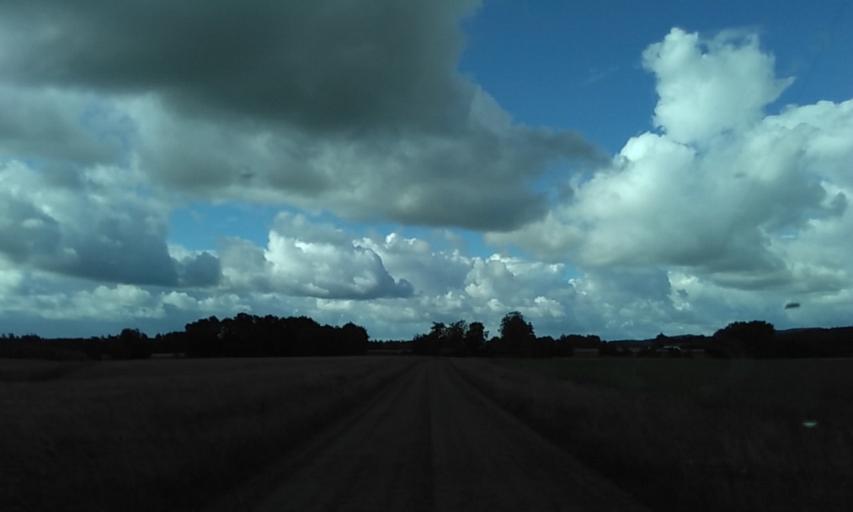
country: SE
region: Vaestra Goetaland
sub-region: Vargarda Kommun
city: Jonstorp
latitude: 57.9930
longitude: 12.6227
